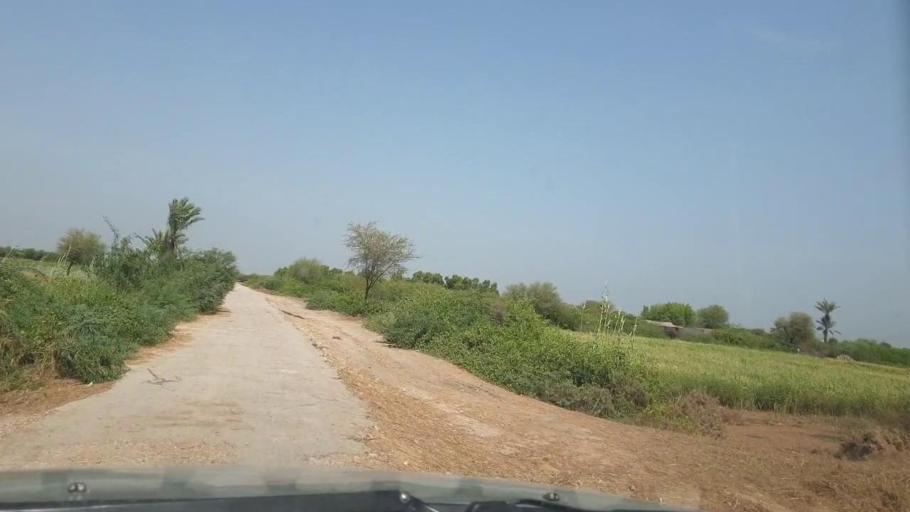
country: PK
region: Sindh
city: Tando Ghulam Ali
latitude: 25.0971
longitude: 68.8021
